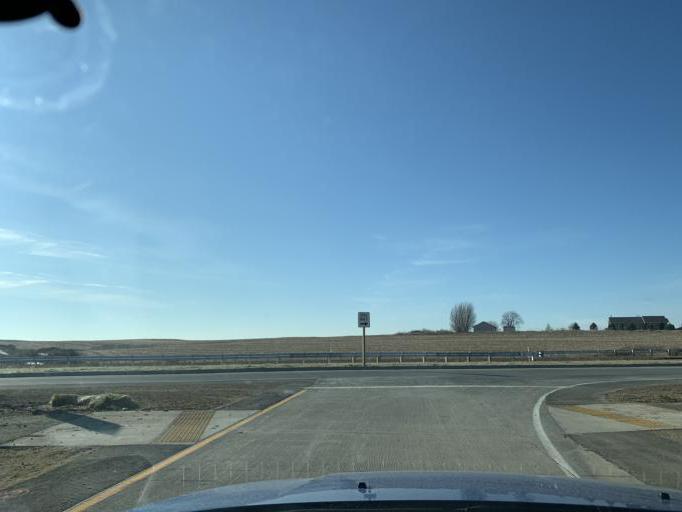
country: US
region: Wisconsin
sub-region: Iowa County
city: Dodgeville
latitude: 42.9377
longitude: -90.1313
